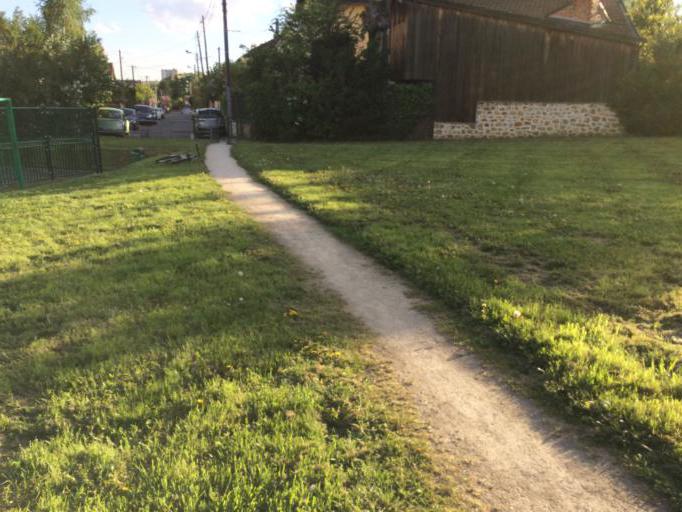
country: FR
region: Ile-de-France
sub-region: Departement de l'Essonne
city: Verrieres-le-Buisson
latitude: 48.7437
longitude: 2.2753
